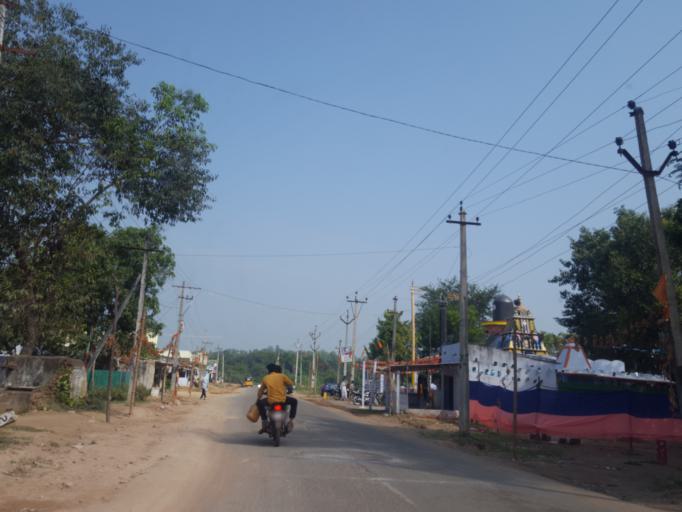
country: IN
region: Telangana
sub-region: Khammam
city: Yellandu
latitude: 17.6049
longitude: 80.3158
